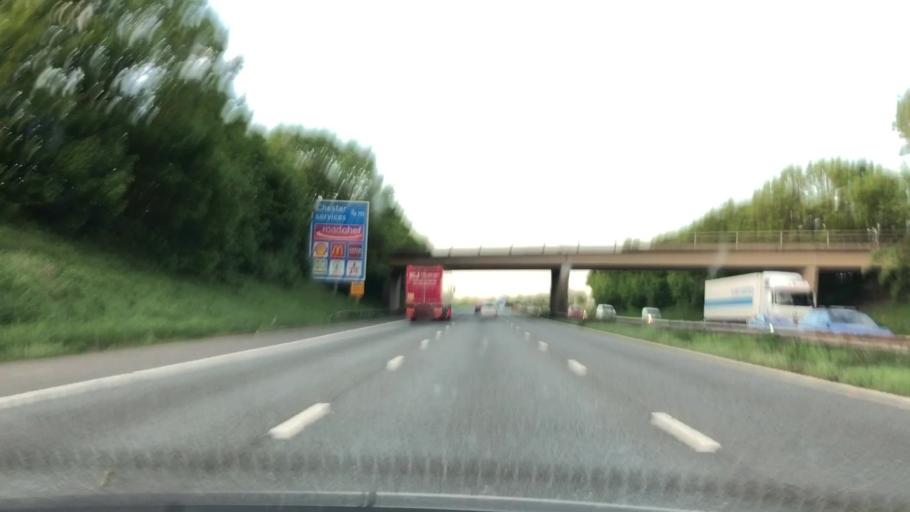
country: GB
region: England
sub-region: Cheshire West and Chester
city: Elton
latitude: 53.2582
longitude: -2.8268
